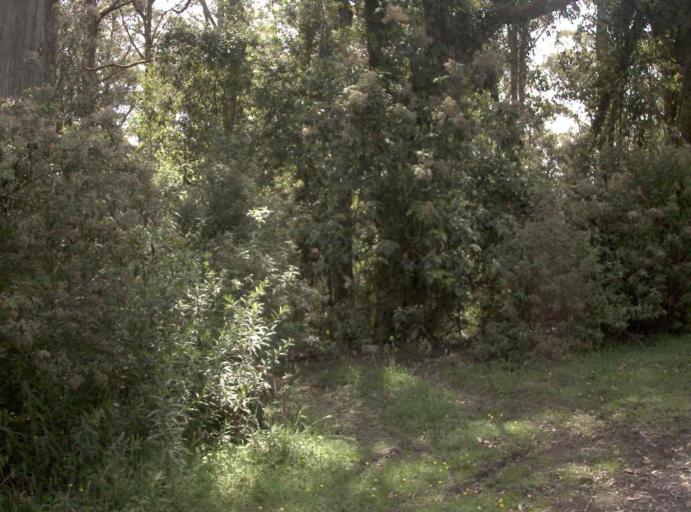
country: AU
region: Victoria
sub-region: Latrobe
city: Morwell
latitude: -38.4366
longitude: 146.5273
